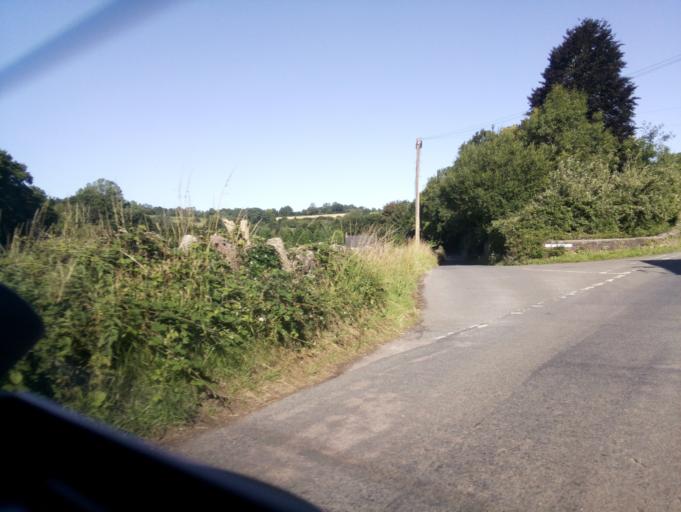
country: GB
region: England
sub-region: Gloucestershire
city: Coleford
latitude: 51.7806
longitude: -2.6448
